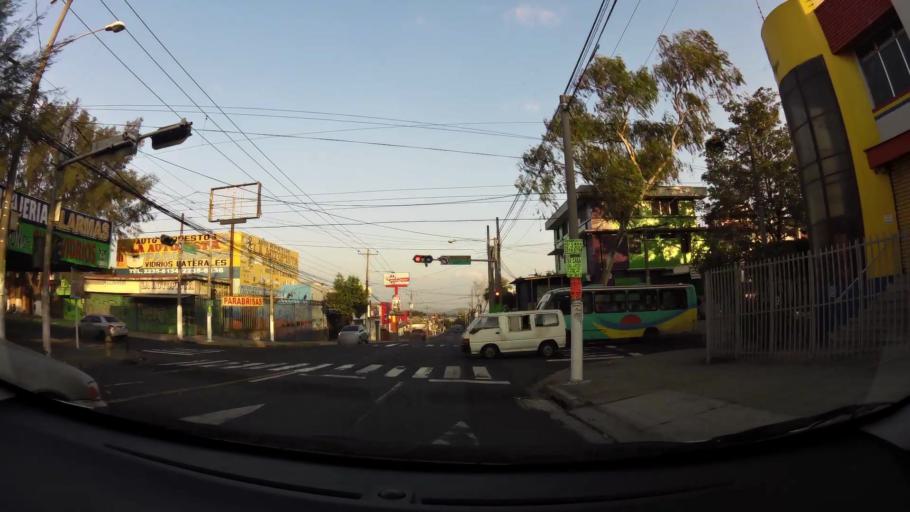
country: SV
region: San Salvador
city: San Salvador
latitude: 13.7140
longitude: -89.2000
